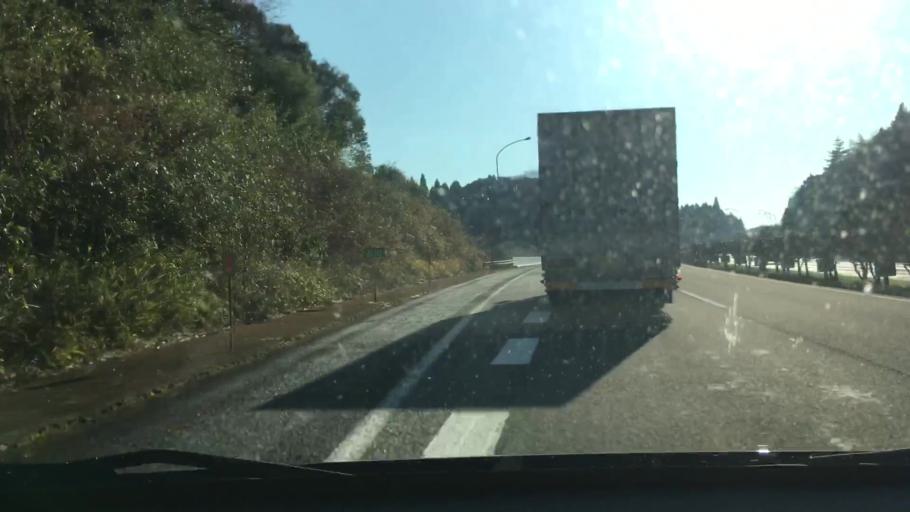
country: JP
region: Kagoshima
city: Kajiki
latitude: 31.8983
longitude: 130.7058
